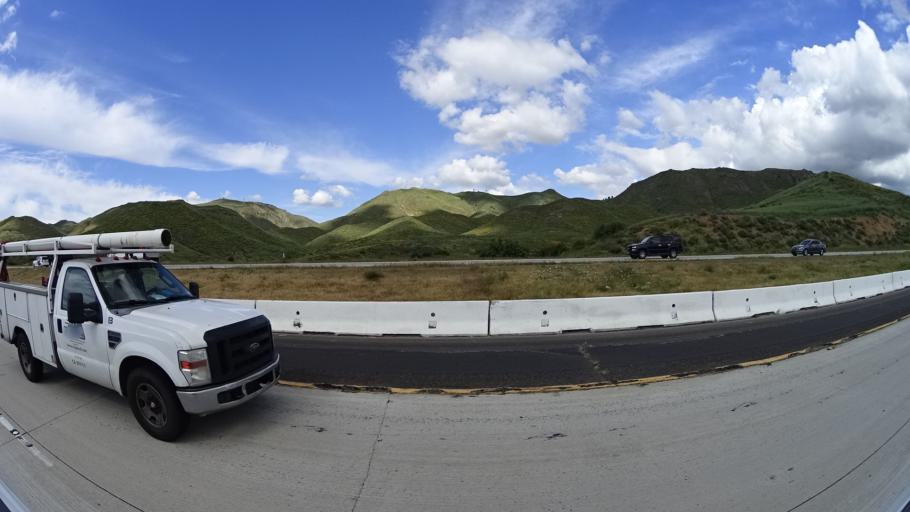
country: US
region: California
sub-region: Riverside County
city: Lake Elsinore
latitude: 33.7249
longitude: -117.3707
